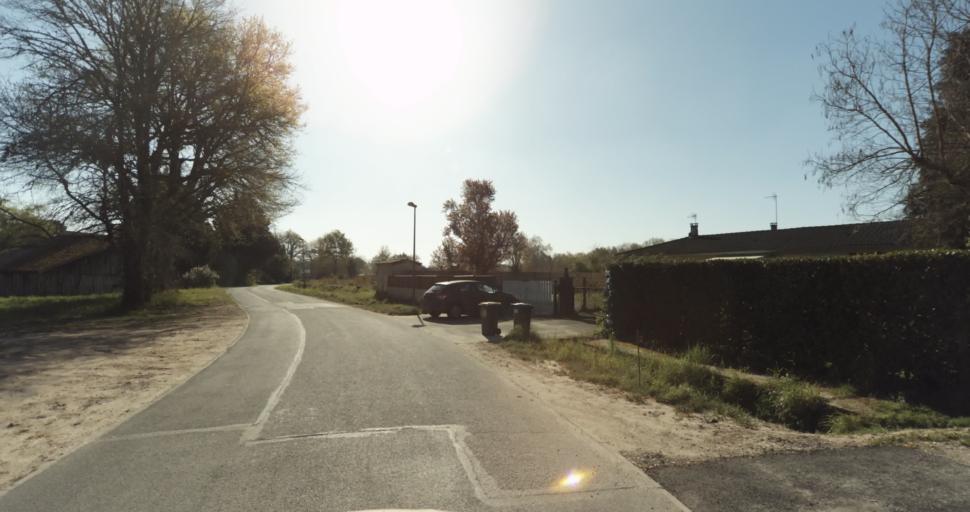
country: FR
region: Aquitaine
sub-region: Departement de la Gironde
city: Martignas-sur-Jalle
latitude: 44.8044
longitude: -0.8430
